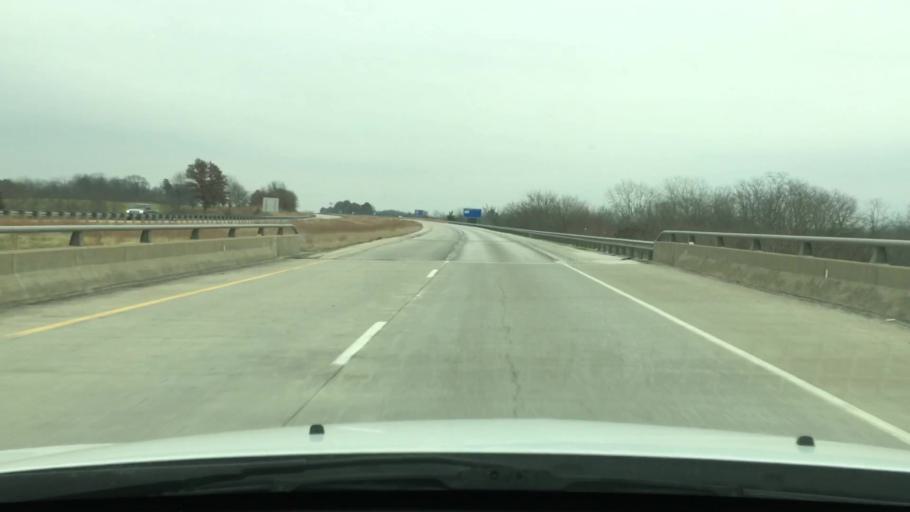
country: US
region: Illinois
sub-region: Morgan County
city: South Jacksonville
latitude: 39.6804
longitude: -90.2675
